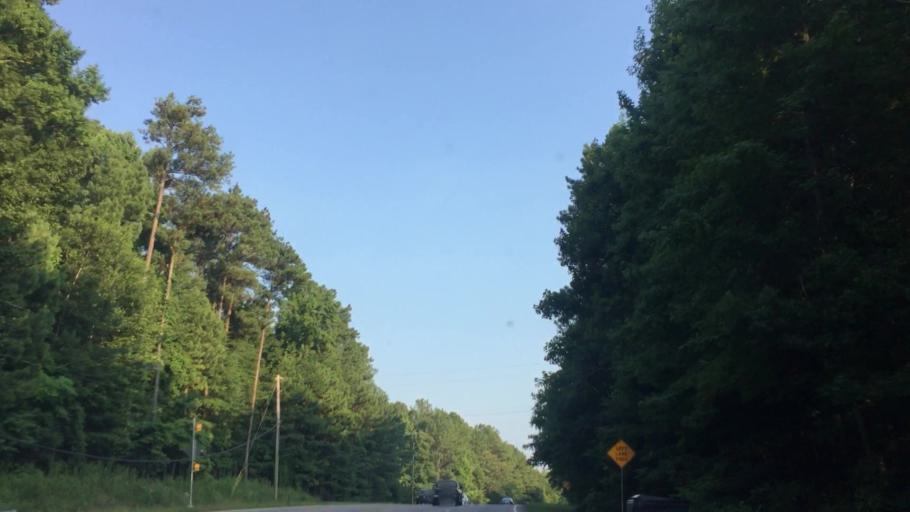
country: US
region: Georgia
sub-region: DeKalb County
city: Pine Mountain
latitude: 33.6439
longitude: -84.1866
